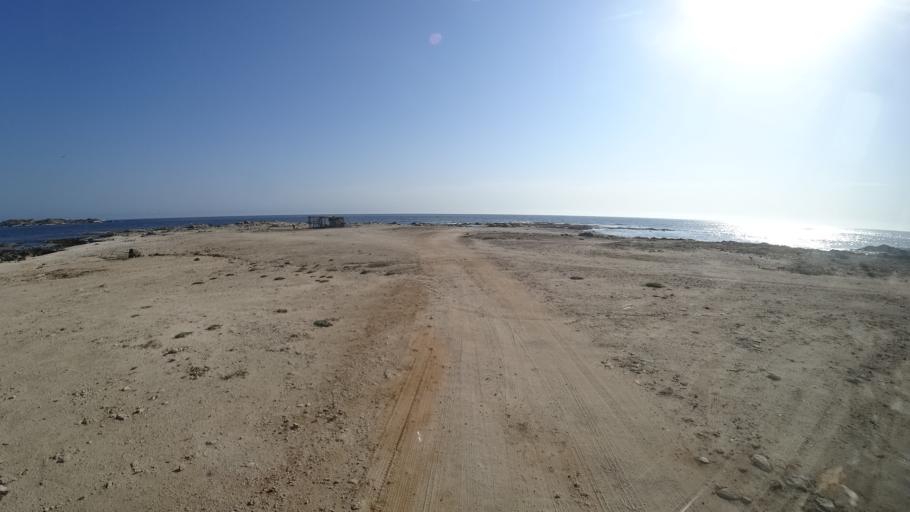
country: OM
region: Zufar
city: Salalah
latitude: 16.9457
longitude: 54.7921
